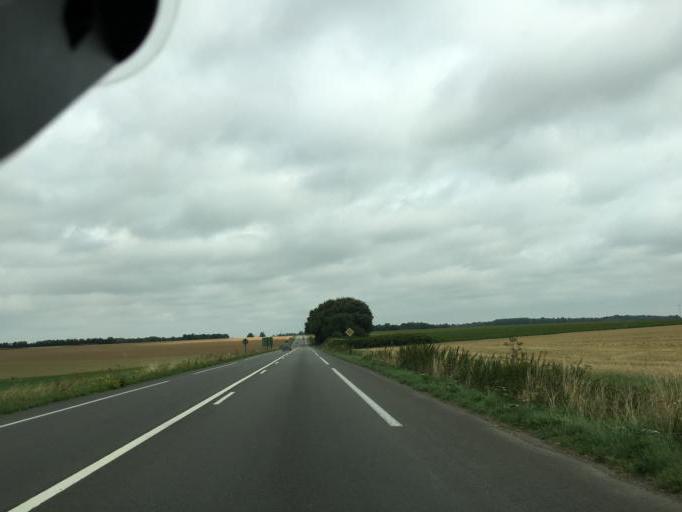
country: FR
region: Nord-Pas-de-Calais
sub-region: Departement du Pas-de-Calais
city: Saint-Pol-sur-Ternoise
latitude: 50.3923
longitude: 2.3537
